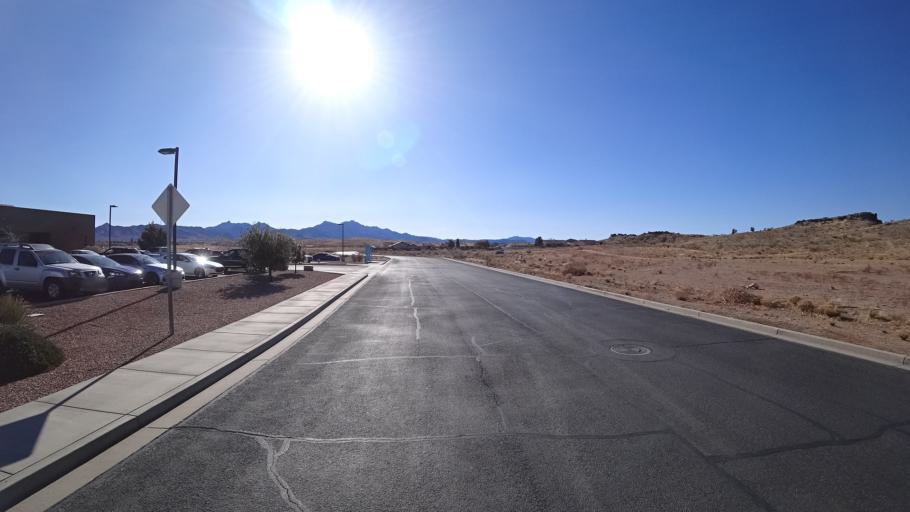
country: US
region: Arizona
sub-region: Mohave County
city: Kingman
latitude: 35.1918
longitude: -114.0270
